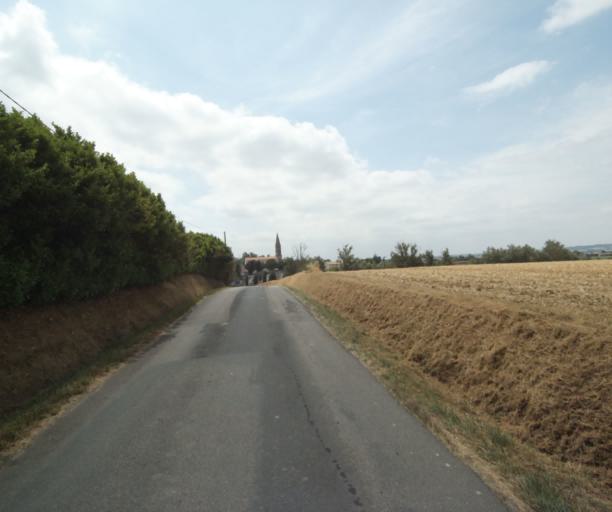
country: FR
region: Midi-Pyrenees
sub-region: Departement de la Haute-Garonne
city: Revel
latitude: 43.4382
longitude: 1.9702
